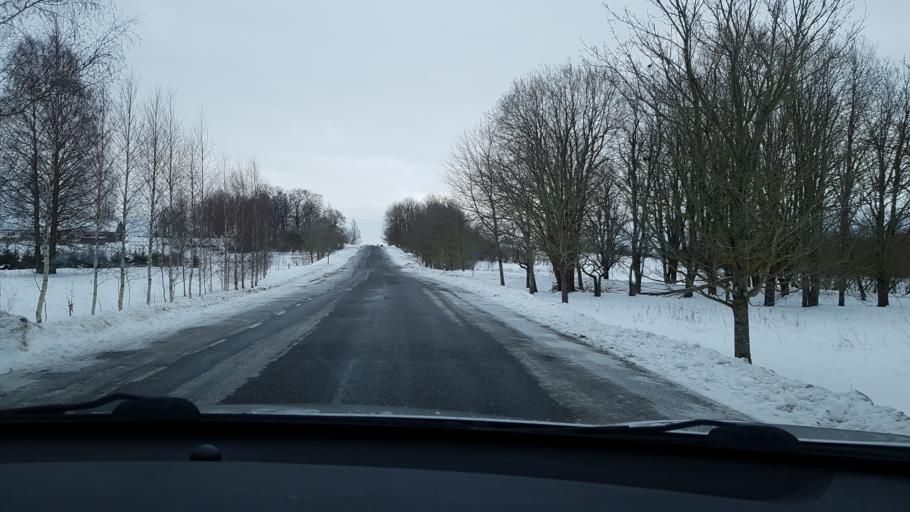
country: EE
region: Jaervamaa
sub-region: Koeru vald
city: Koeru
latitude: 58.9833
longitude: 25.9883
